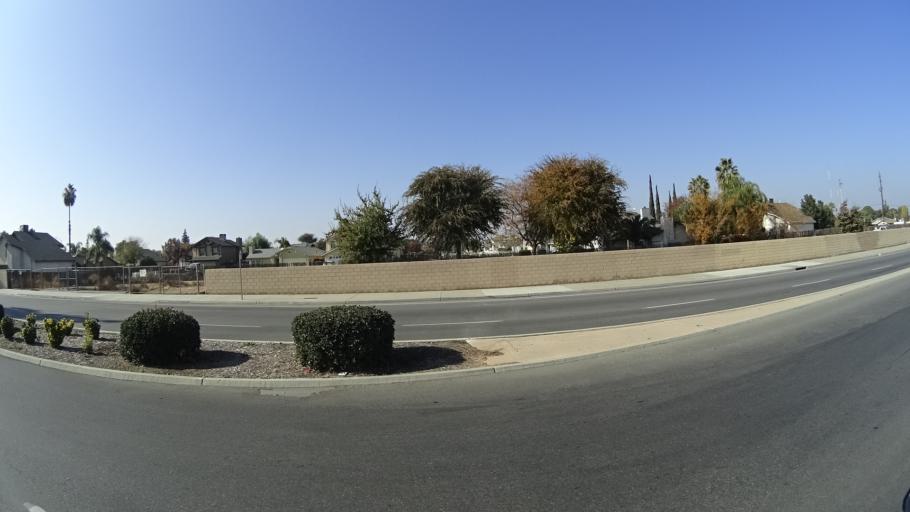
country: US
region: California
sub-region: Kern County
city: Greenfield
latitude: 35.3023
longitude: -119.0389
